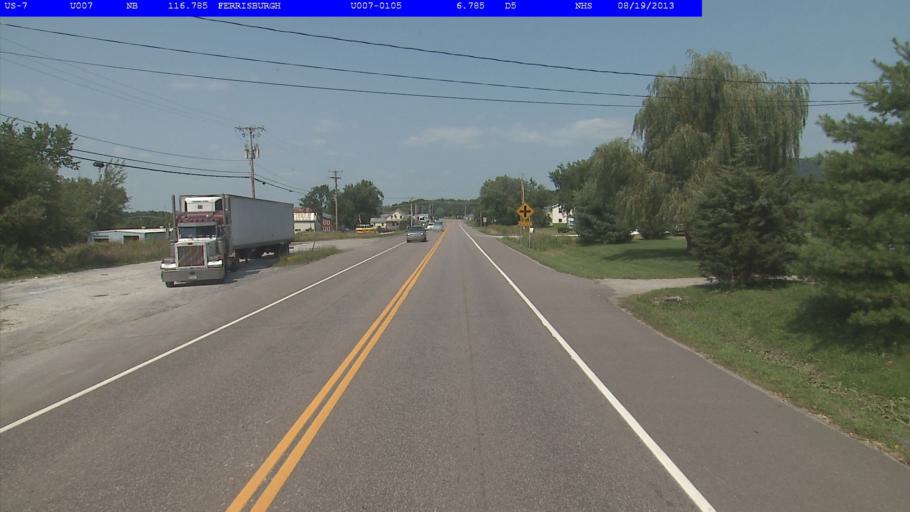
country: US
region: Vermont
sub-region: Addison County
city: Vergennes
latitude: 44.2556
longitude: -73.2278
